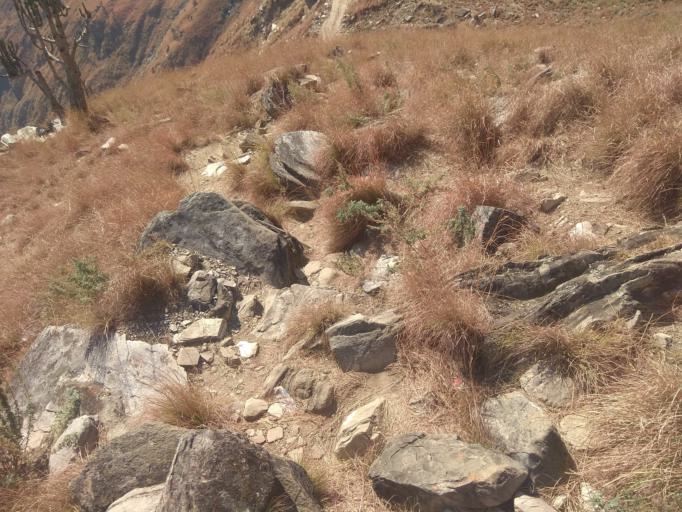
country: NP
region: Mid Western
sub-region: Karnali Zone
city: Jumla
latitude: 29.3079
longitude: 81.7466
